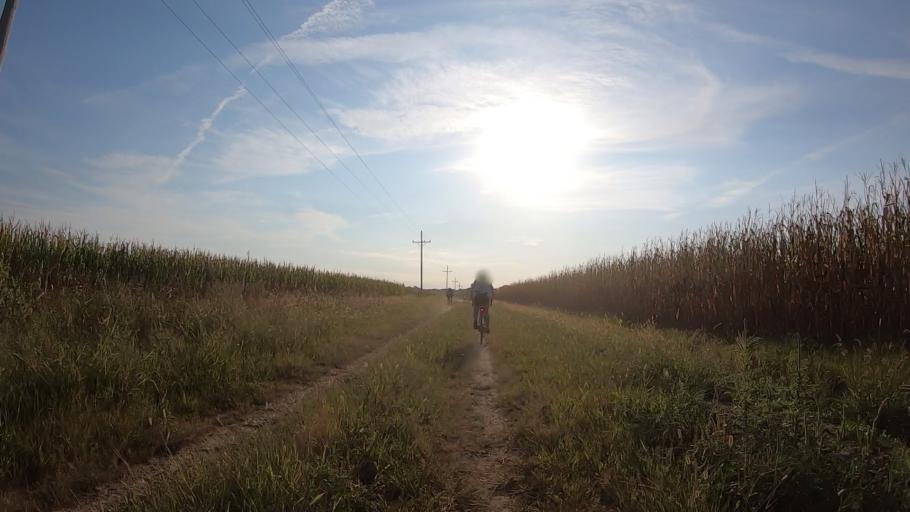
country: US
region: Kansas
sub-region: Marshall County
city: Blue Rapids
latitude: 39.7118
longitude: -96.7868
